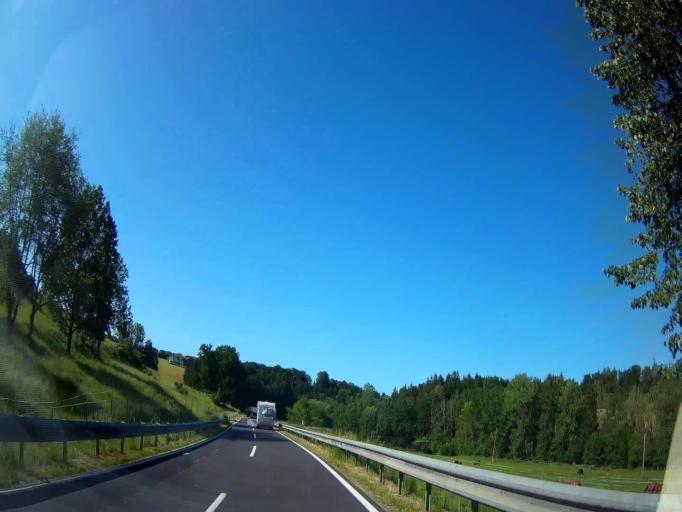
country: AT
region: Salzburg
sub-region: Politischer Bezirk Salzburg-Umgebung
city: Dorfbeuern
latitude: 48.1283
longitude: 13.0113
